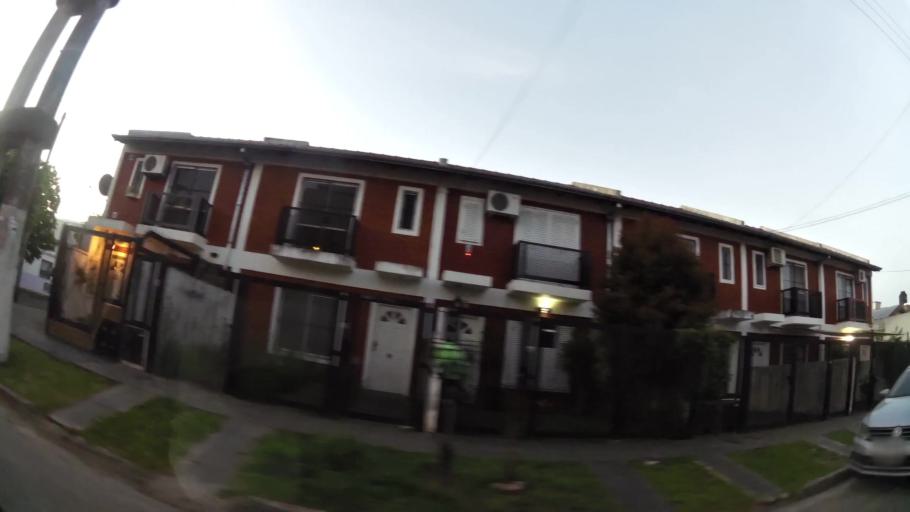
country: AR
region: Buenos Aires
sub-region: Partido de Quilmes
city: Quilmes
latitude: -34.7749
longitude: -58.2106
